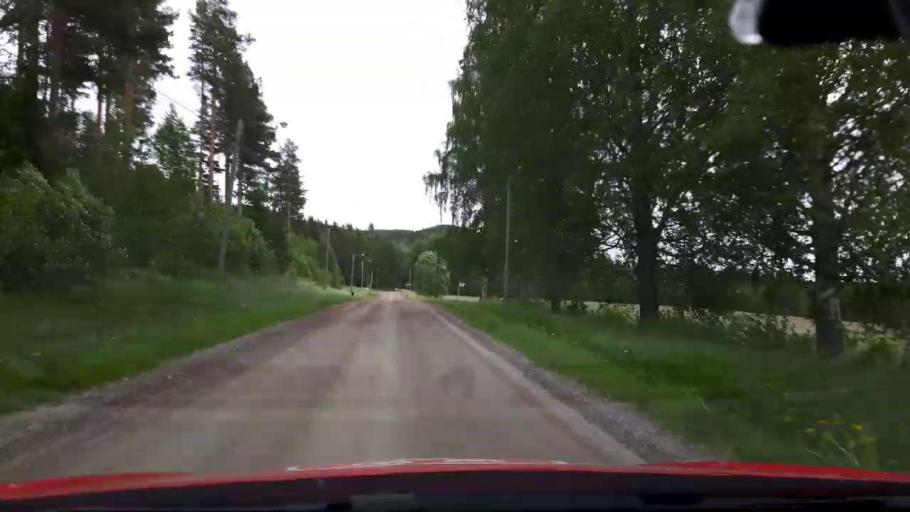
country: SE
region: Jaemtland
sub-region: Ragunda Kommun
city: Hammarstrand
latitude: 63.1770
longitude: 16.1922
